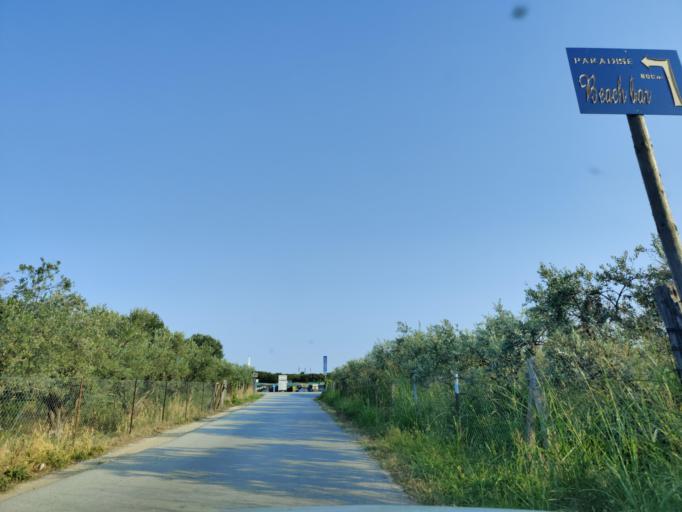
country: GR
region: East Macedonia and Thrace
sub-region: Nomos Kavalas
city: Nea Peramos
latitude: 40.8144
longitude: 24.2877
